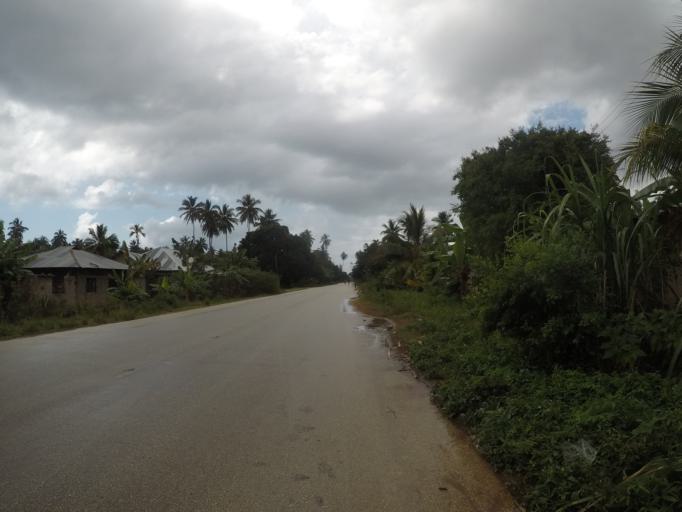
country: TZ
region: Zanzibar North
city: Mkokotoni
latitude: -5.9778
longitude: 39.1961
